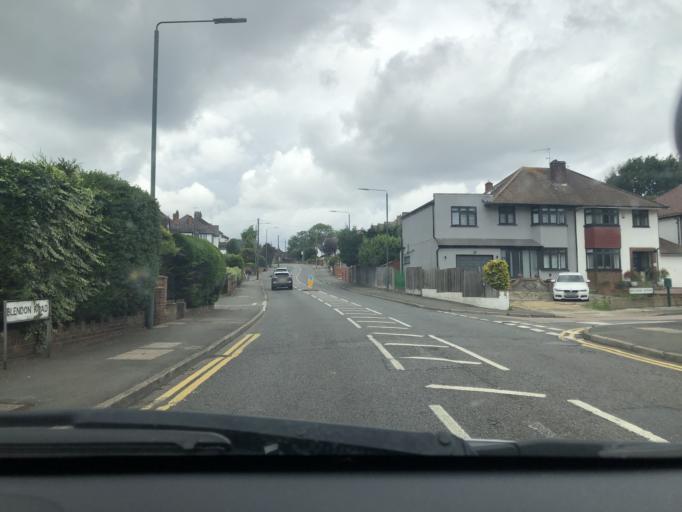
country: GB
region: England
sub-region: Greater London
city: Bexley
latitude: 51.4460
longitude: 0.1308
